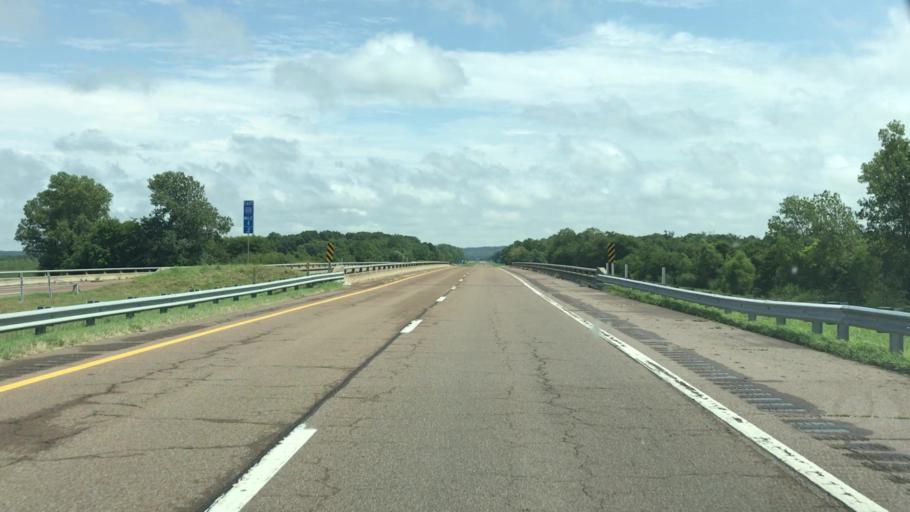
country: US
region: Missouri
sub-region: Pemiscot County
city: Caruthersville
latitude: 36.0855
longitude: -89.5513
